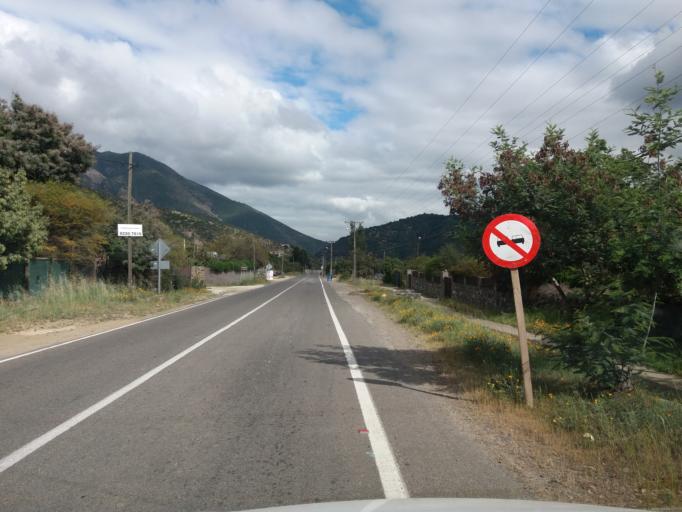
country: CL
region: Valparaiso
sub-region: Provincia de Marga Marga
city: Limache
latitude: -33.0544
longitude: -71.0908
